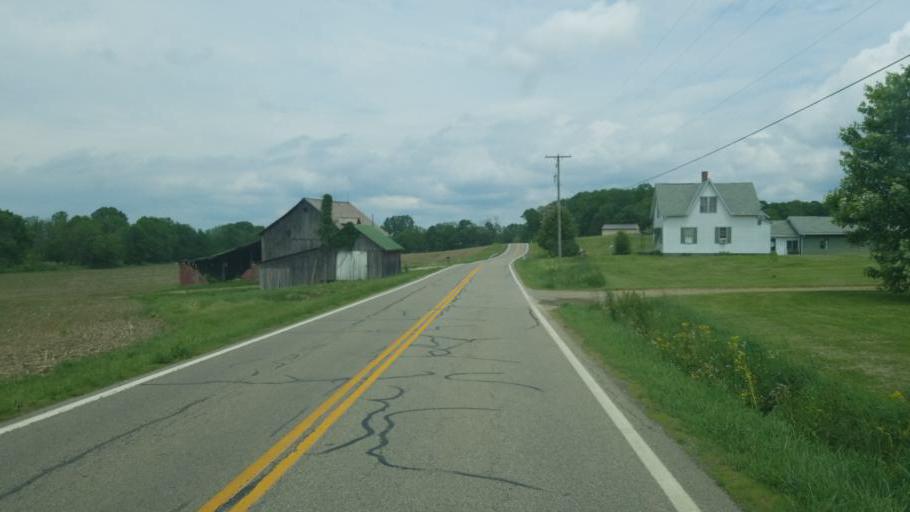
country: US
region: Ohio
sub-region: Perry County
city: Thornport
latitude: 39.9018
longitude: -82.3843
